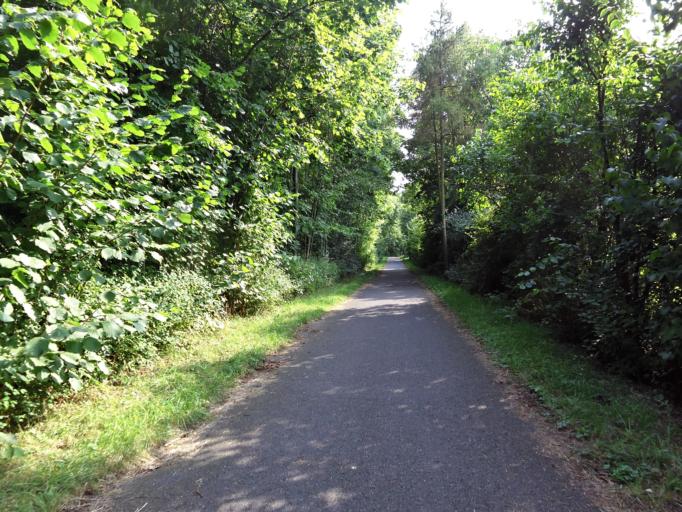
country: DE
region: Saxony
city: Leipzig
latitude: 51.3837
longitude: 12.3875
